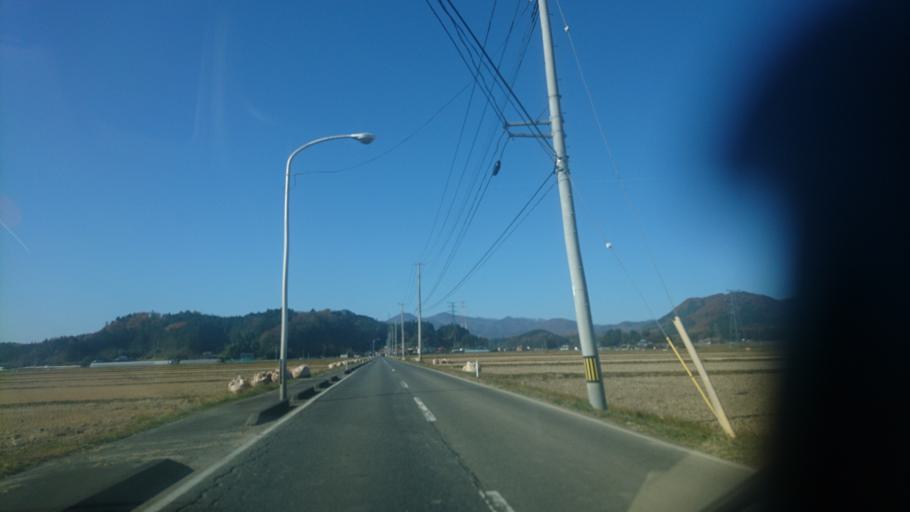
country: JP
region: Miyagi
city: Tomiya
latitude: 38.4099
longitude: 140.8778
